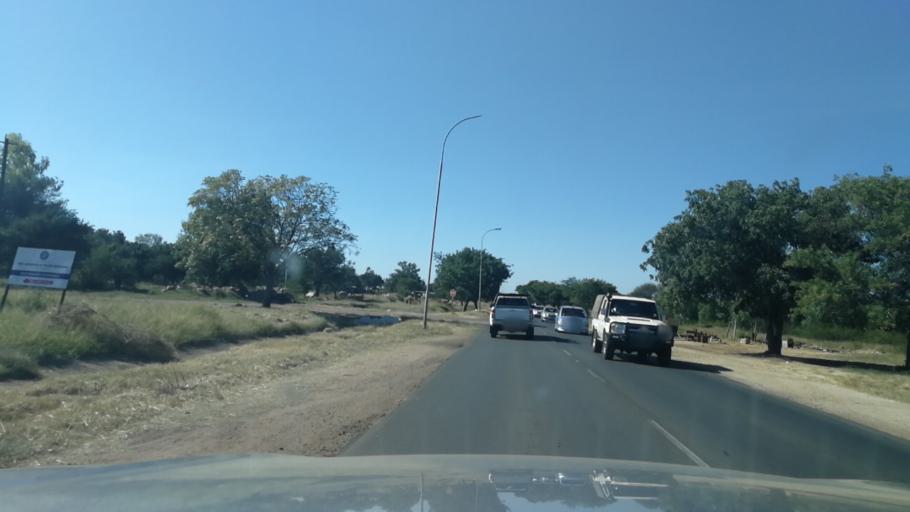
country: BW
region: South East
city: Gaborone
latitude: -24.6919
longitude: 25.8987
